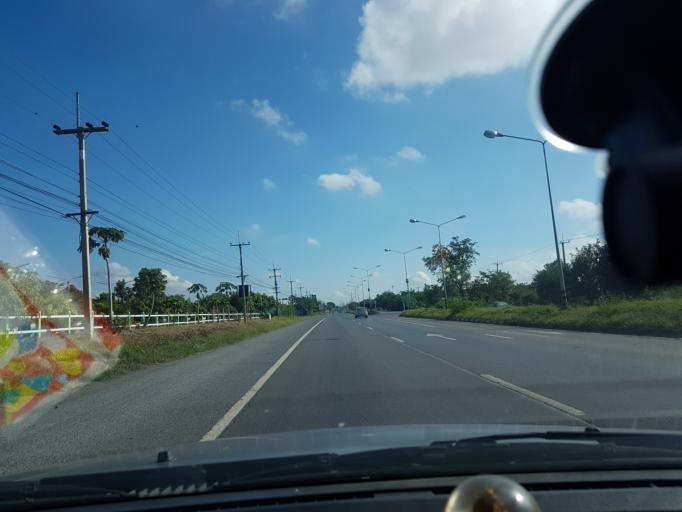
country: TH
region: Lop Buri
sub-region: Amphoe Tha Luang
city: Tha Luang
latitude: 15.0723
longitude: 100.9883
